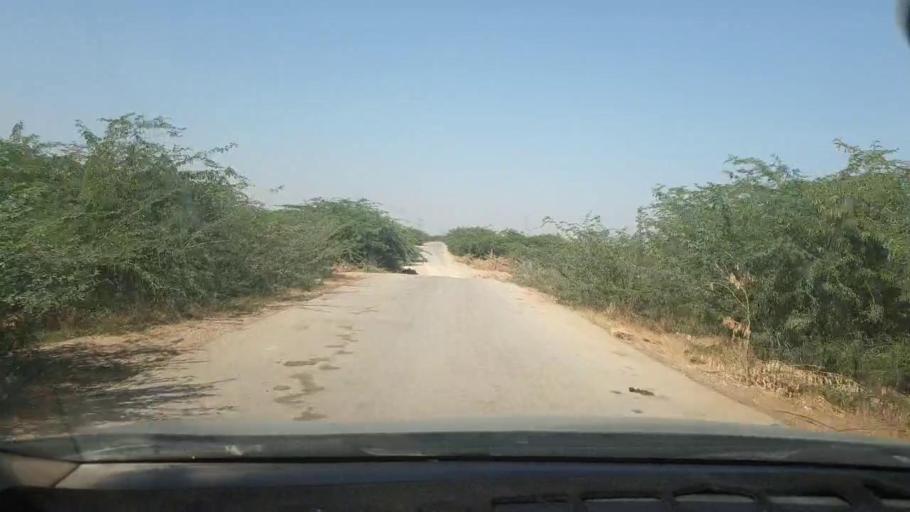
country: PK
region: Sindh
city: Malir Cantonment
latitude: 25.1589
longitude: 67.1646
